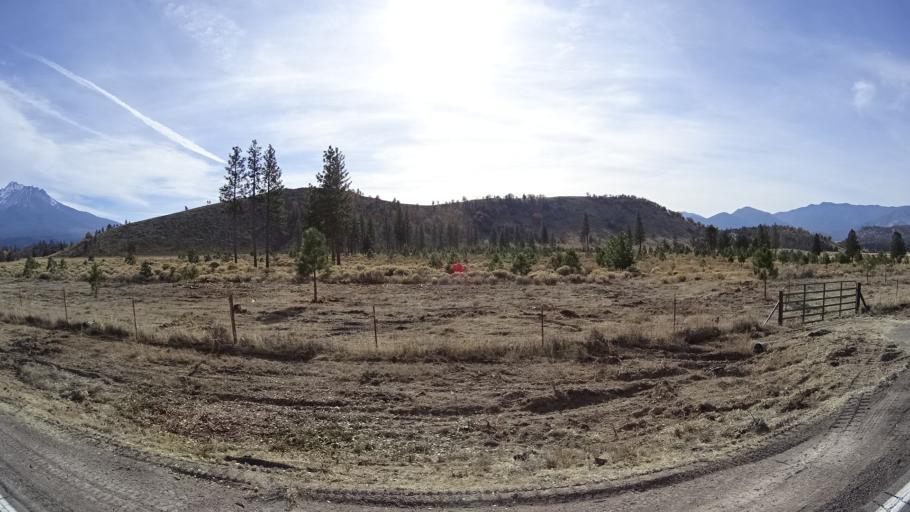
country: US
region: California
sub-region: Siskiyou County
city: Weed
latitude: 41.4940
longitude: -122.3960
